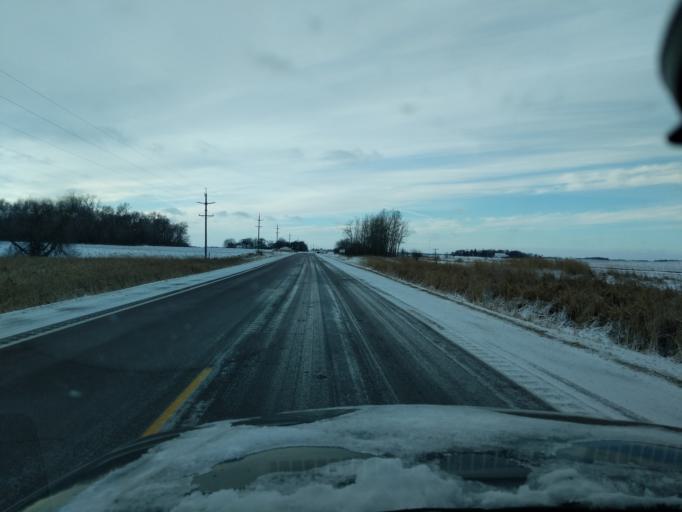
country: US
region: Minnesota
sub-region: Renville County
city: Hector
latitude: 44.7243
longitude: -94.5286
